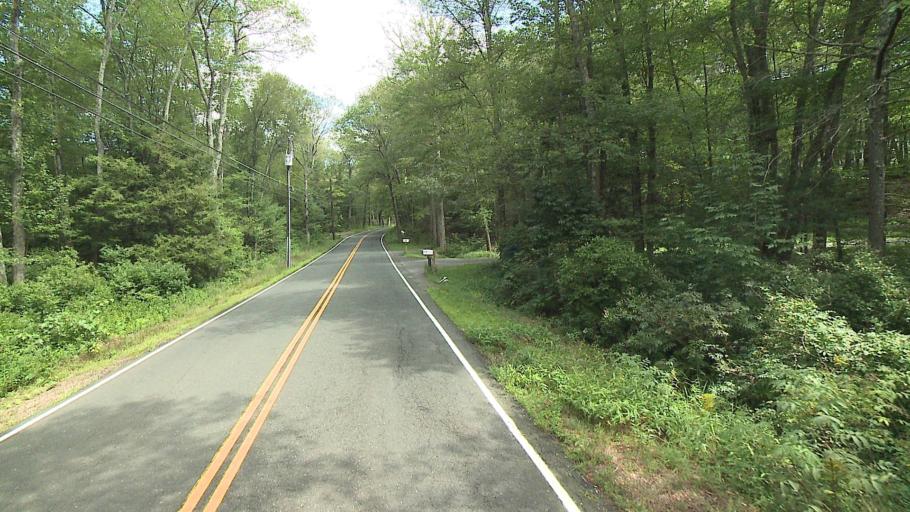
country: US
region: Connecticut
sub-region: Tolland County
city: Crystal Lake
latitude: 41.9342
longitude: -72.3509
